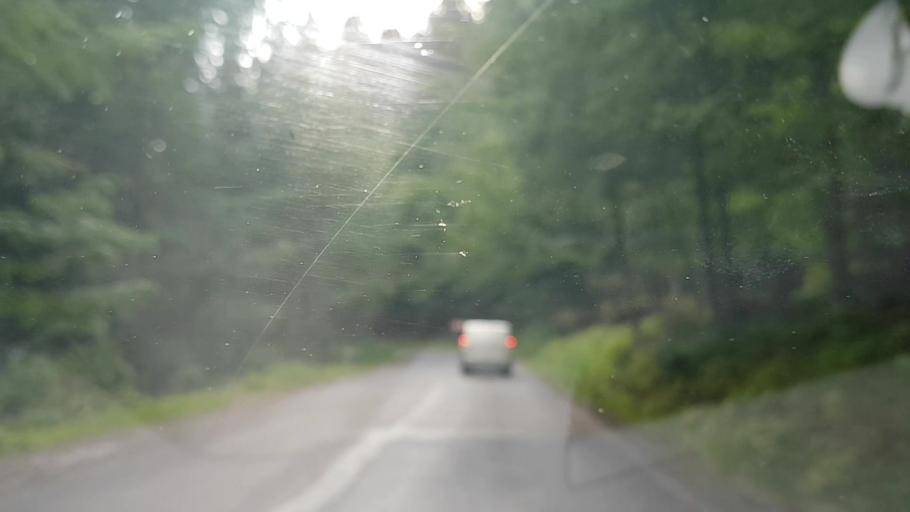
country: RO
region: Harghita
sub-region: Comuna Varsag
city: Varsag
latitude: 46.6658
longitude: 25.3115
